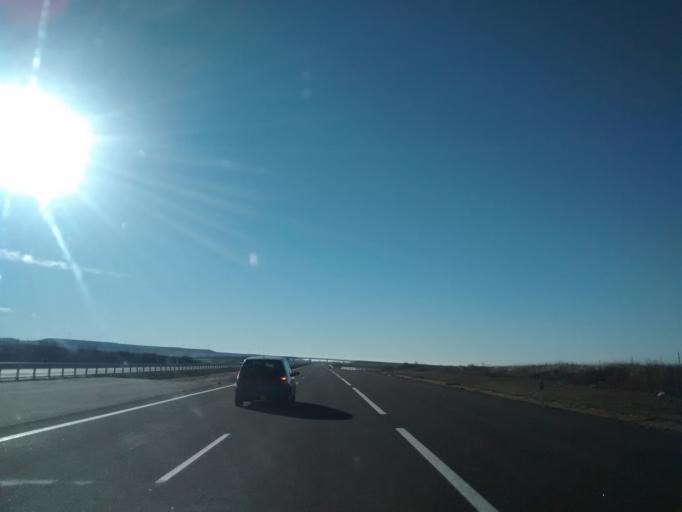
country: ES
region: Castille and Leon
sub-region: Provincia de Palencia
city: Santa Cruz de Boedo
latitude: 42.5209
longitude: -4.3834
